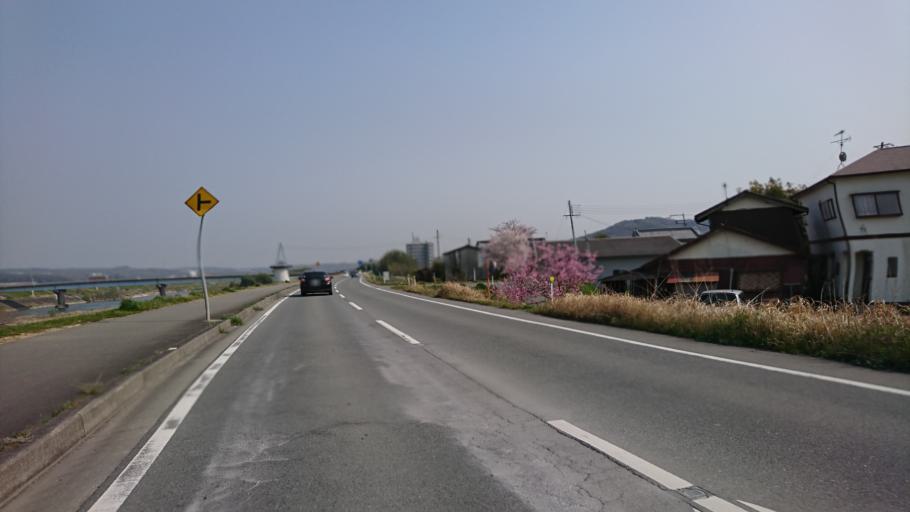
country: JP
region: Hyogo
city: Ono
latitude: 34.8383
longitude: 134.9167
